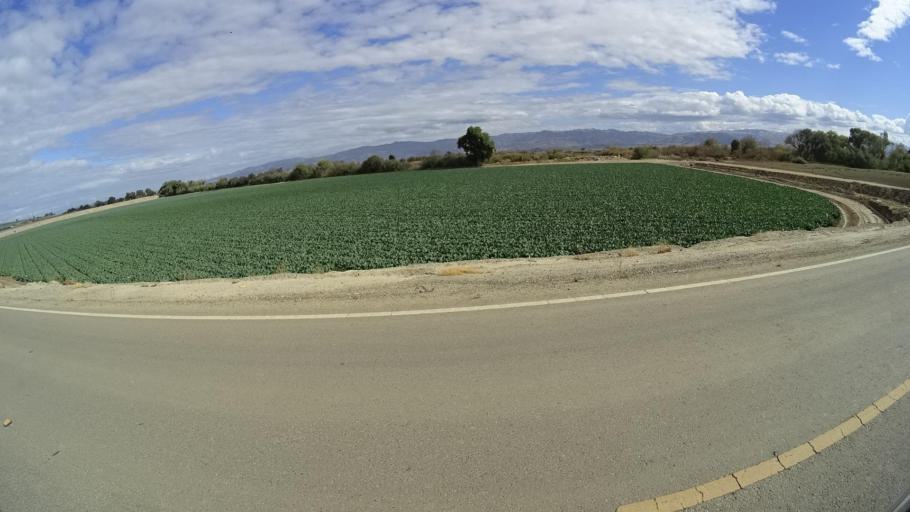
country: US
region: California
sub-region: Monterey County
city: Chualar
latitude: 36.5329
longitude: -121.5425
